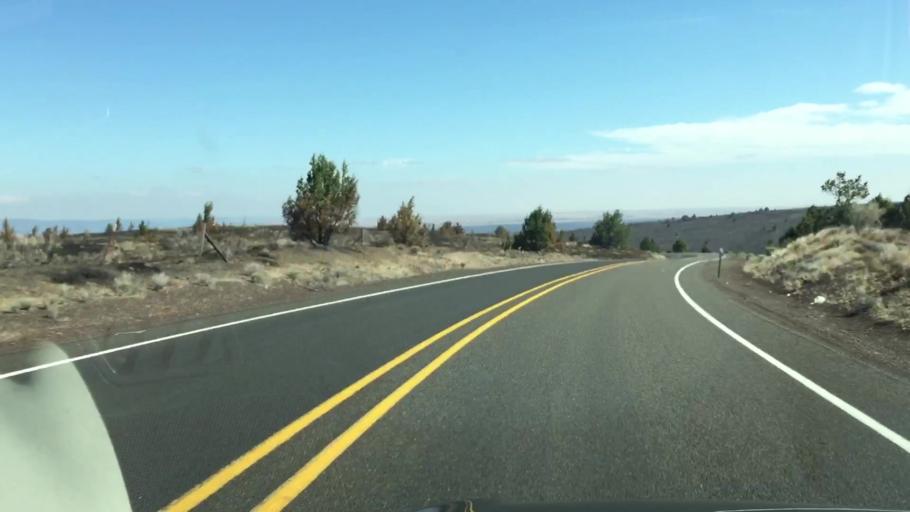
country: US
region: Oregon
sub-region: Jefferson County
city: Warm Springs
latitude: 45.0642
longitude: -121.0253
